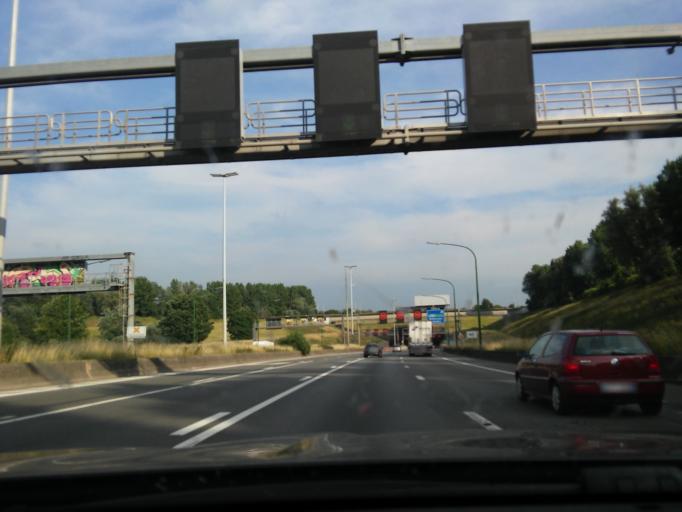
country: BE
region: Flanders
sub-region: Provincie Antwerpen
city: Hoboken
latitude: 51.2109
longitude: 4.3655
